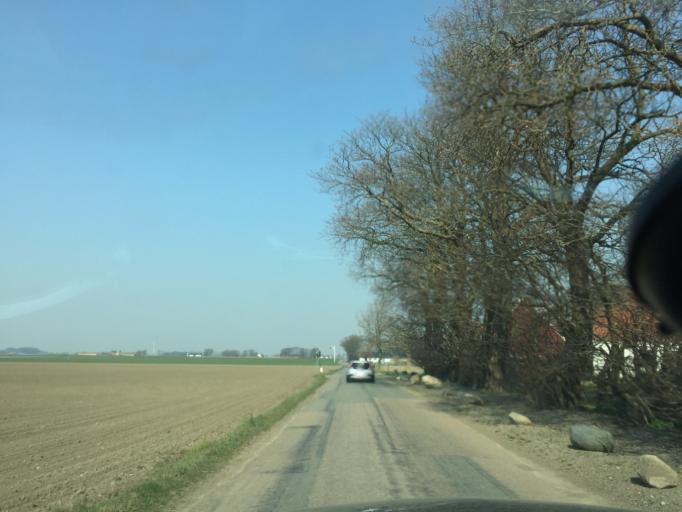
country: SE
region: Skane
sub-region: Simrishamns Kommun
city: Simrishamn
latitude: 55.4441
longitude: 14.2190
